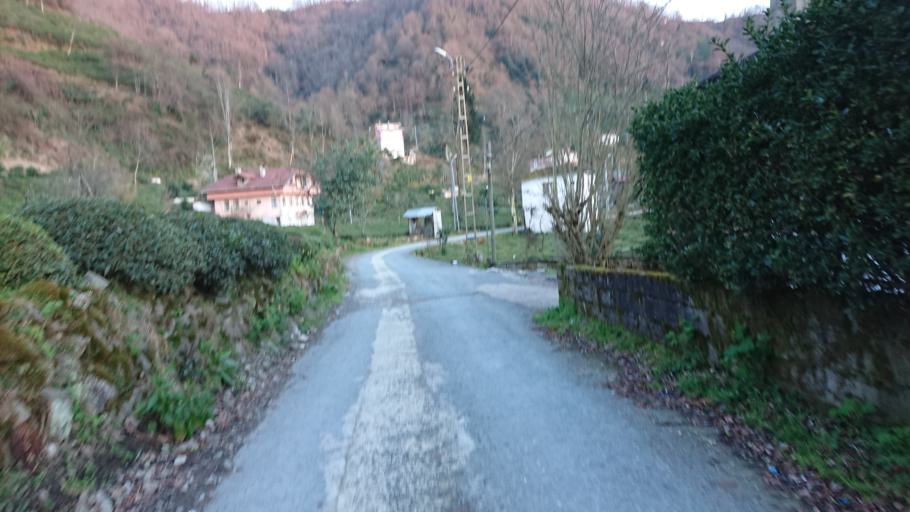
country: TR
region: Rize
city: Rize
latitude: 40.9823
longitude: 40.4947
